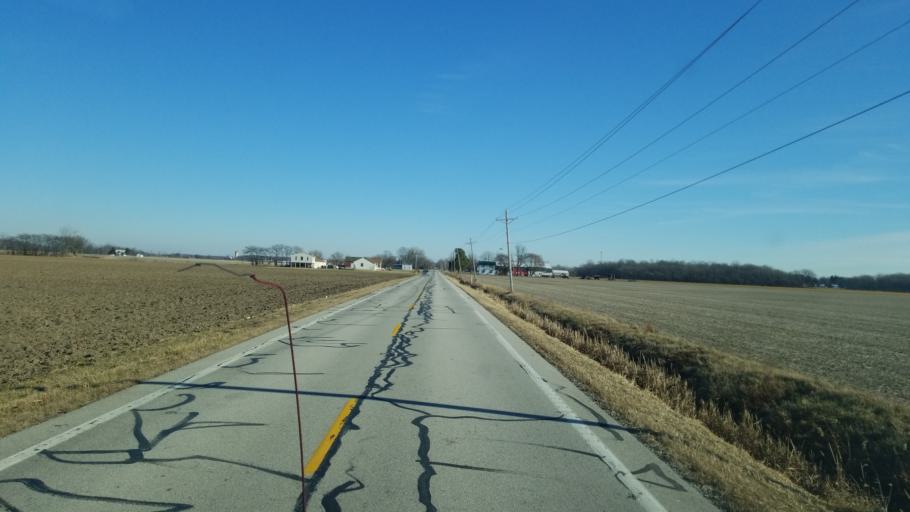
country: US
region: Ohio
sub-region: Wood County
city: Luckey
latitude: 41.4570
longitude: -83.5065
